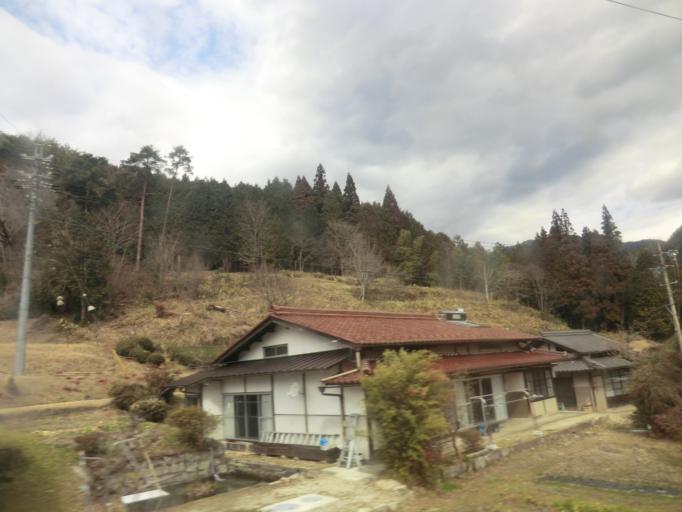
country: JP
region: Gifu
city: Nakatsugawa
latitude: 35.5881
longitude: 137.5434
